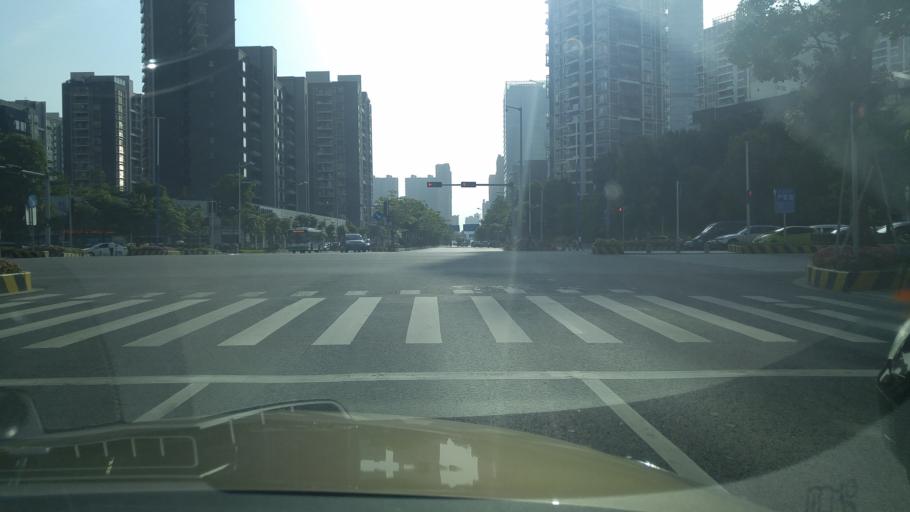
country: CN
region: Guangdong
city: Foshan
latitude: 23.0652
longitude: 113.1502
